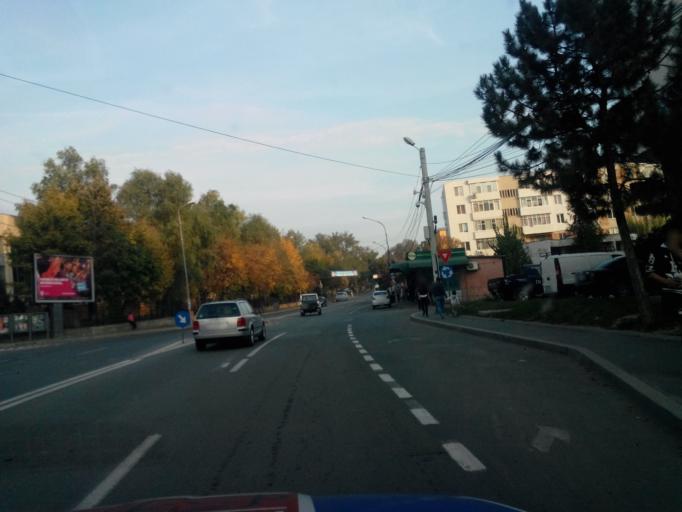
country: RO
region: Tulcea
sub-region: Municipiul Tulcea
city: Tulcea
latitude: 45.1803
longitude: 28.7806
